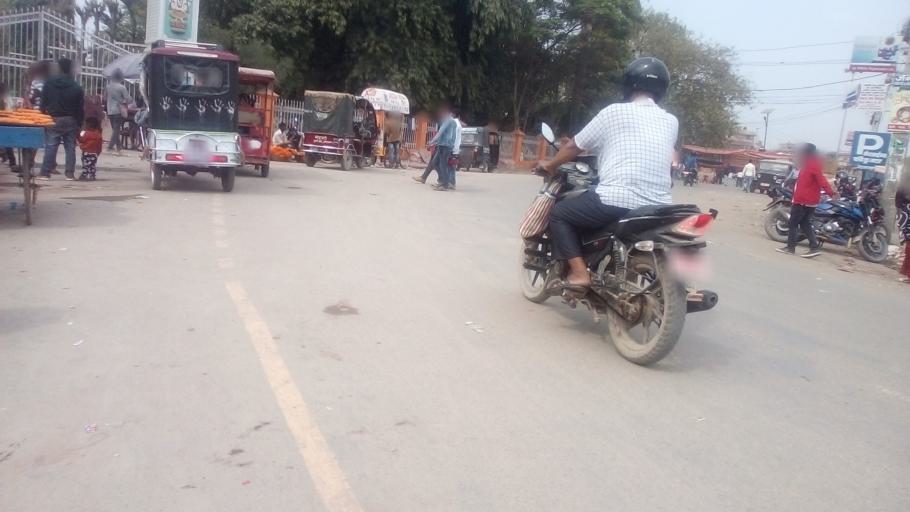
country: NP
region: Central Region
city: Janakpur
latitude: 26.7309
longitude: 85.9261
